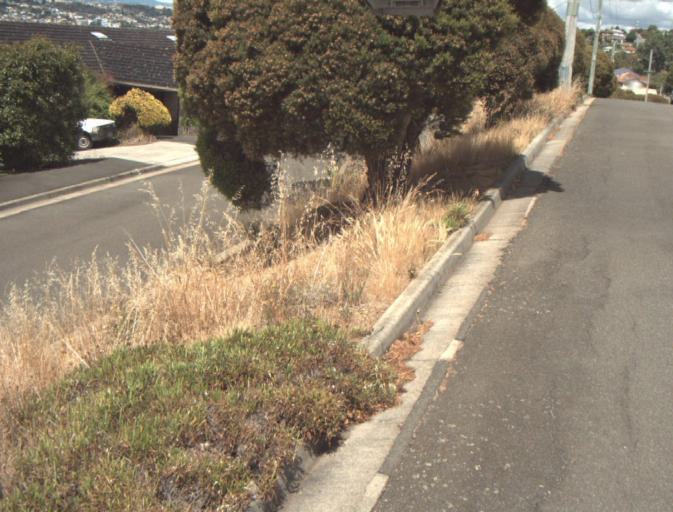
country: AU
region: Tasmania
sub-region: Launceston
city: Launceston
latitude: -41.4317
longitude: 147.1149
